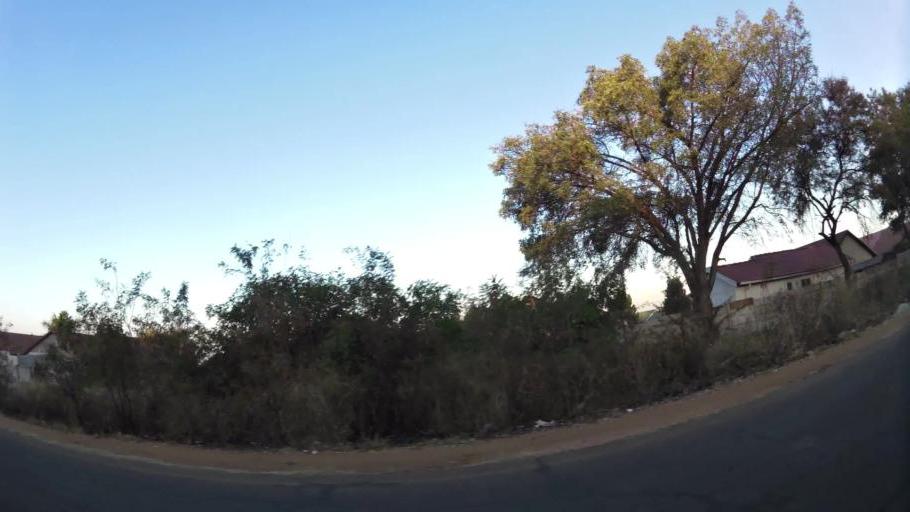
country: ZA
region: North-West
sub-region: Bojanala Platinum District Municipality
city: Rustenburg
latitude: -25.6380
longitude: 27.2005
